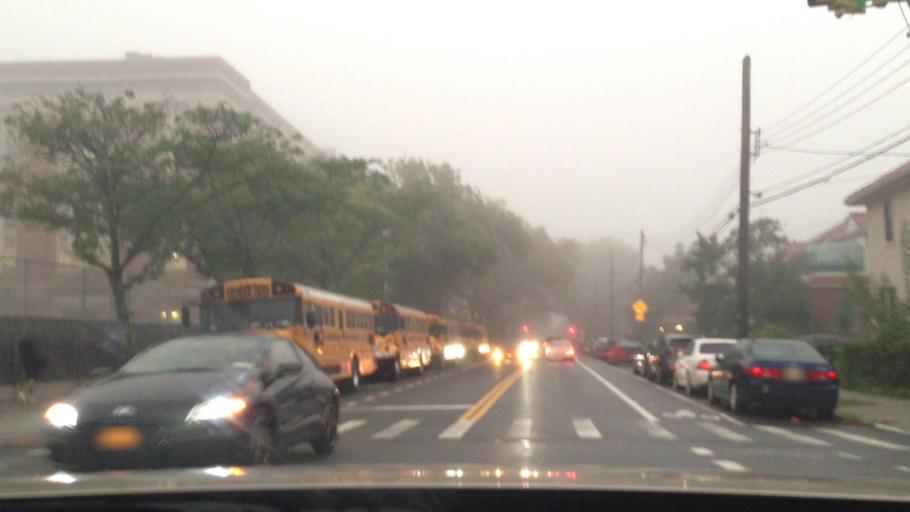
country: US
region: New York
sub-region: Kings County
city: Brooklyn
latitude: 40.6115
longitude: -73.9489
